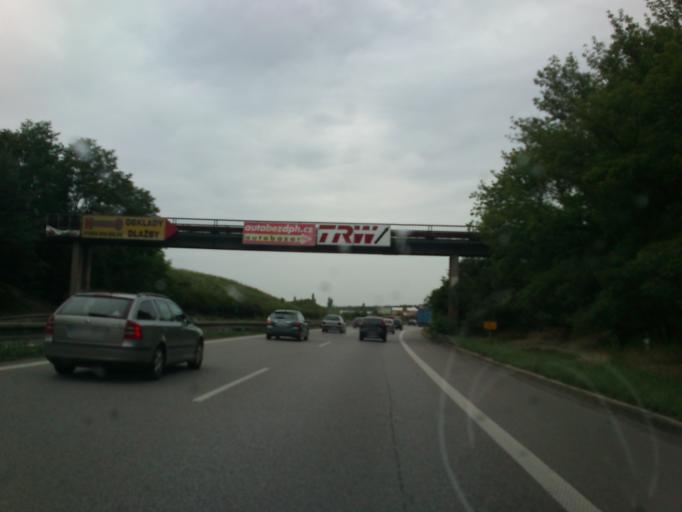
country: CZ
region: Central Bohemia
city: Brandys nad Labem-Stara Boleslav
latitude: 50.1978
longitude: 14.6913
